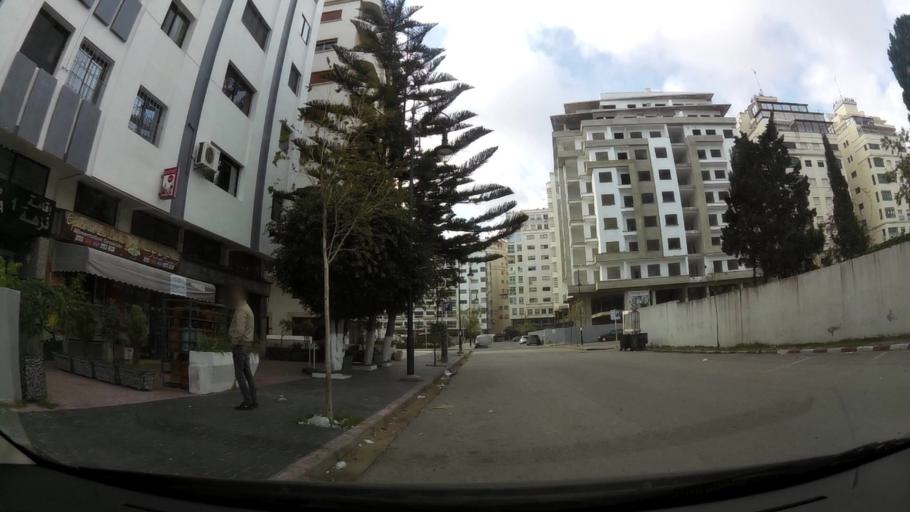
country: CL
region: Biobio
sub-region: Provincia de Concepcion
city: Concepcion
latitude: -36.7933
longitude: -73.0707
